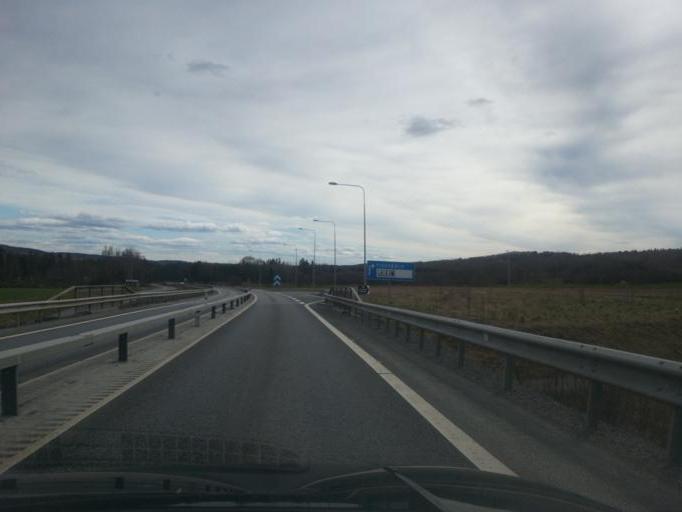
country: SE
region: Joenkoeping
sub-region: Habo Kommun
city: Habo
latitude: 57.8869
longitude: 14.1029
